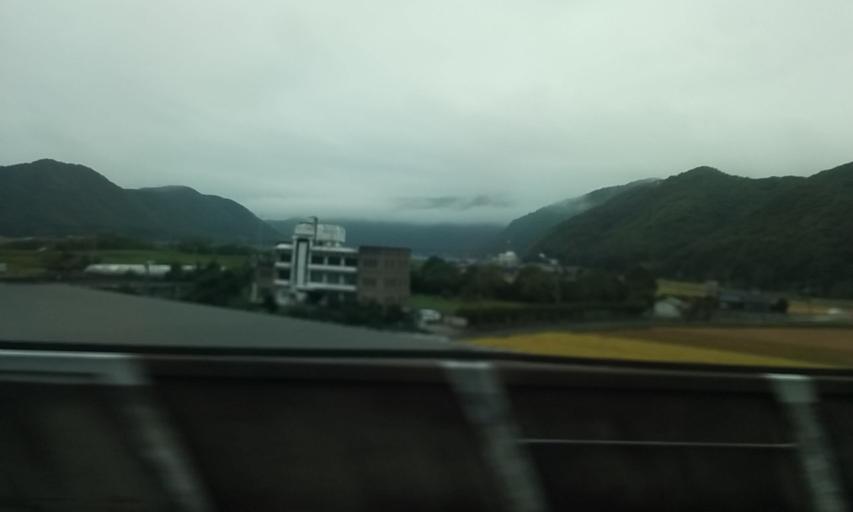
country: JP
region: Okayama
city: Okayama-shi
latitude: 34.7262
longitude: 134.1069
